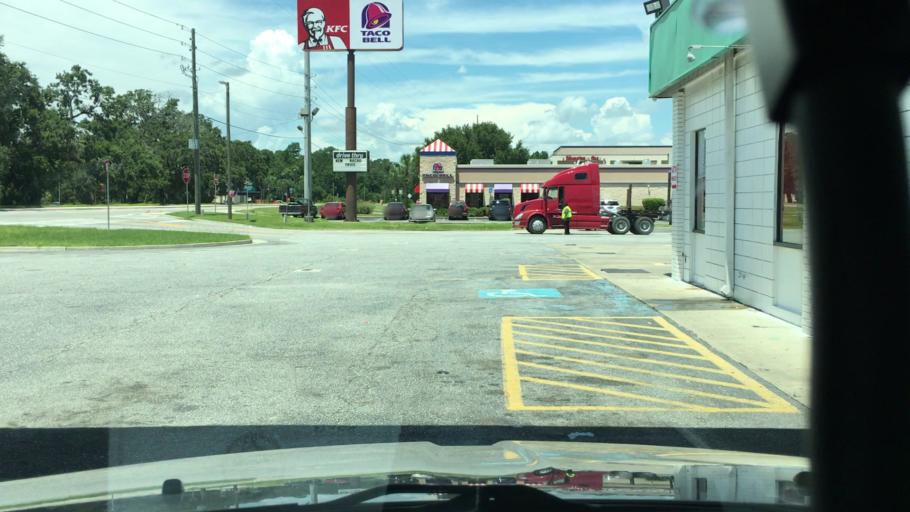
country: US
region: Georgia
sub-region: McIntosh County
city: Darien
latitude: 31.3988
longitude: -81.4505
